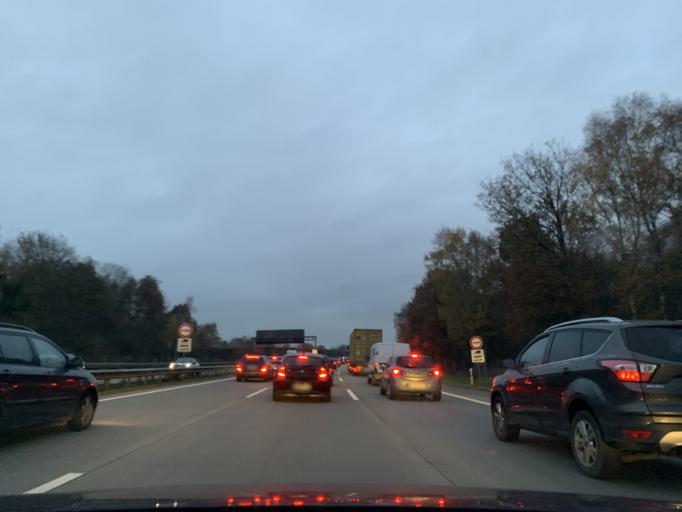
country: DE
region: Lower Saxony
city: Ritterhude
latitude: 53.1540
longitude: 8.7250
